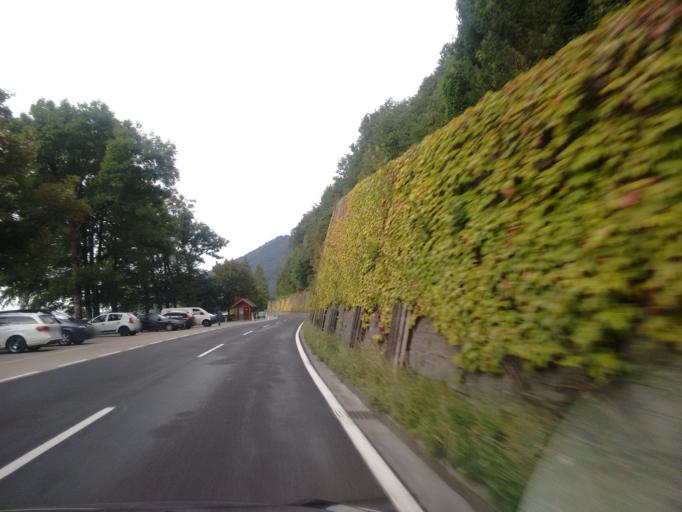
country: AT
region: Upper Austria
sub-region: Politischer Bezirk Vocklabruck
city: Steinbach am Attersee
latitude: 47.8636
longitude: 13.5627
